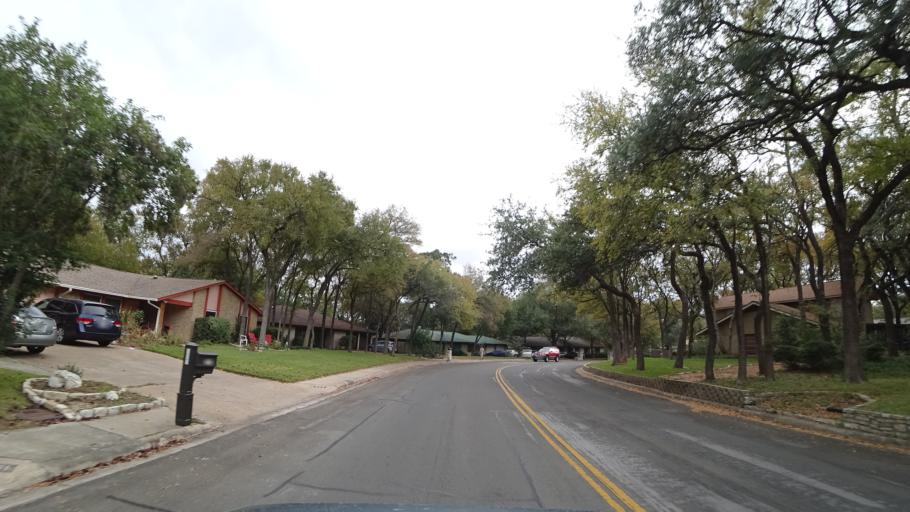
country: US
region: Texas
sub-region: Williamson County
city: Round Rock
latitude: 30.5053
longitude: -97.6944
